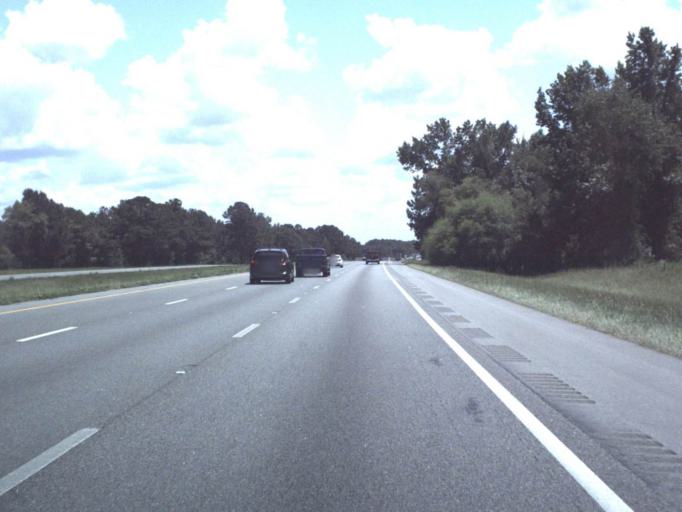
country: US
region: Florida
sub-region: Hamilton County
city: Jasper
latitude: 30.5442
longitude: -83.0756
